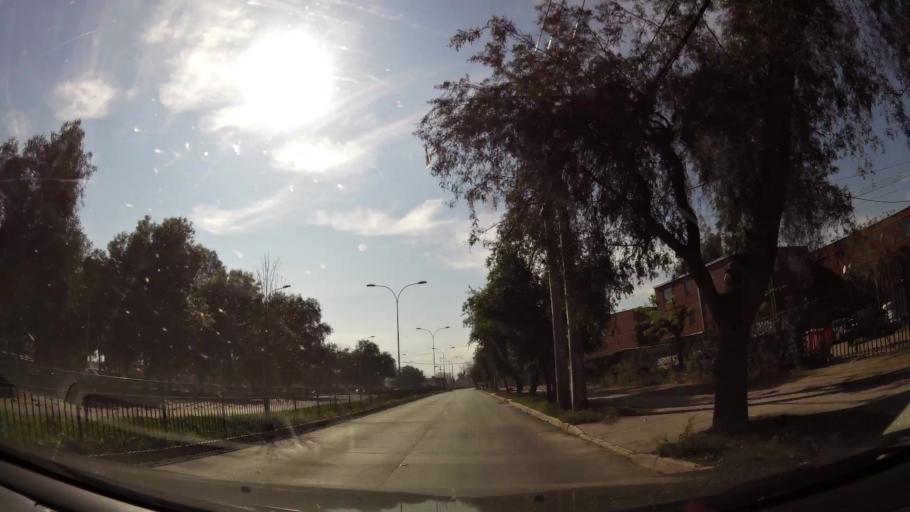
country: CL
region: Santiago Metropolitan
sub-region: Provincia de Santiago
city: Santiago
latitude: -33.3957
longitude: -70.6549
